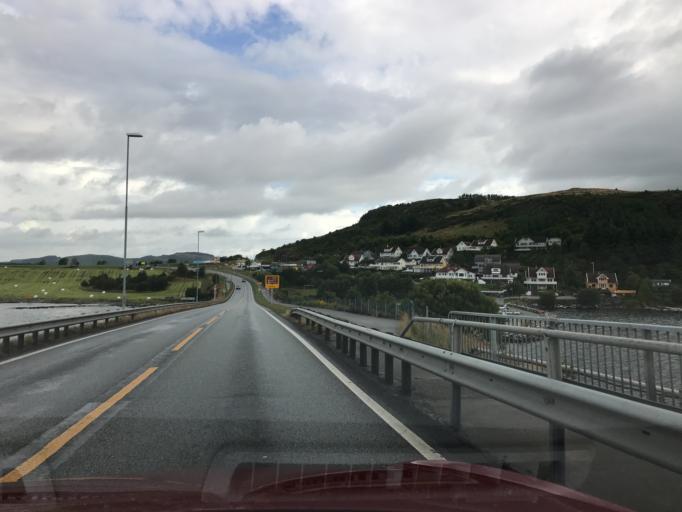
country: NO
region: Rogaland
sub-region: Rennesoy
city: Vikevag
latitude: 59.0602
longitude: 5.6773
